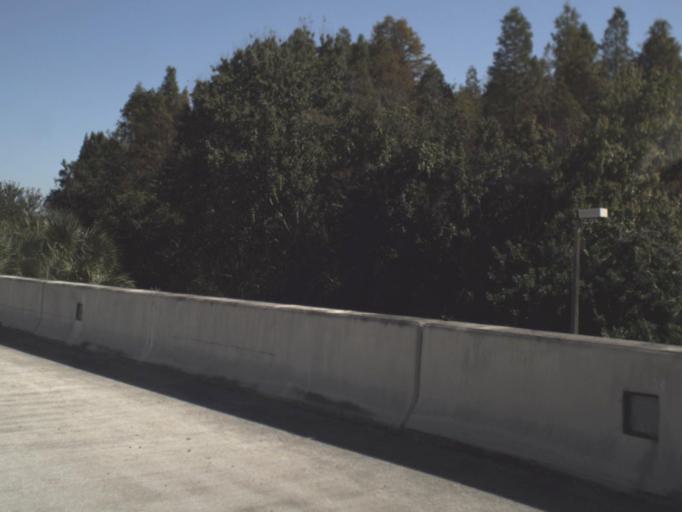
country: US
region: Florida
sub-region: Hillsborough County
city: Cheval
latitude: 28.1500
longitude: -82.5407
